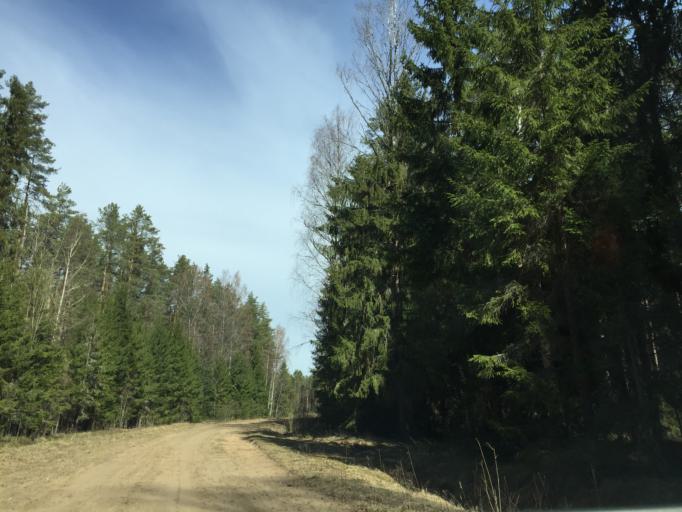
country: LV
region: Strenci
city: Seda
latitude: 57.6389
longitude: 25.8376
